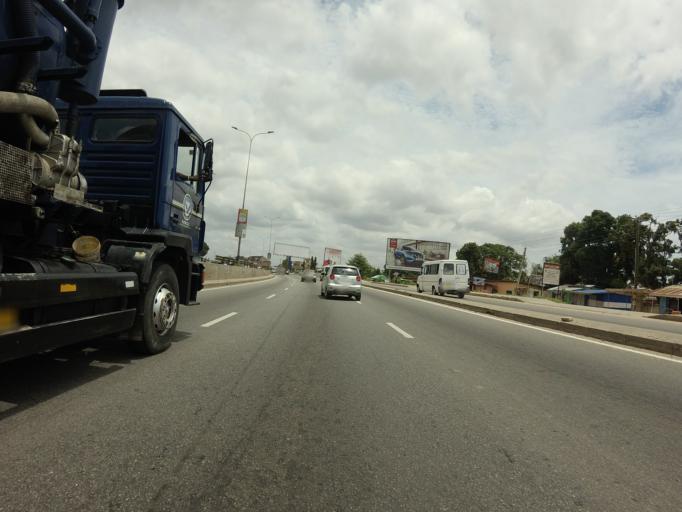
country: GH
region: Greater Accra
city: Gbawe
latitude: 5.5602
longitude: -0.2920
